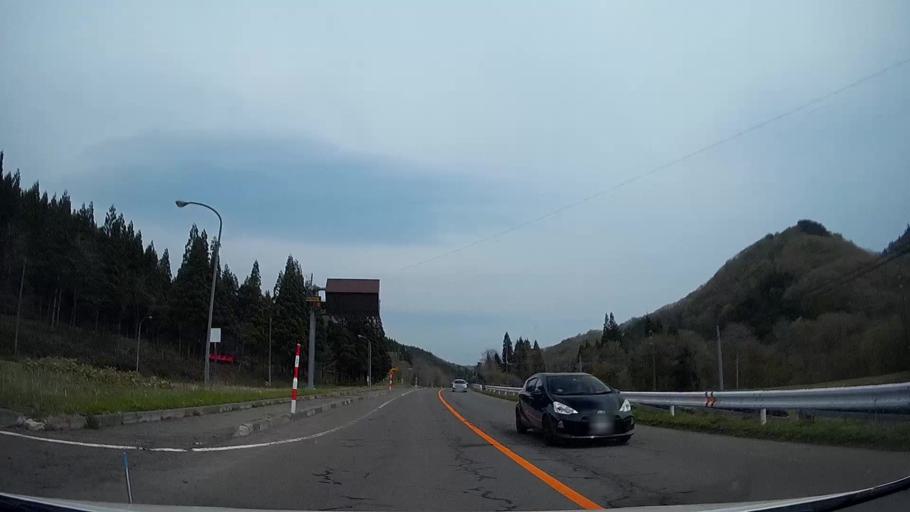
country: JP
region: Akita
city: Hanawa
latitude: 40.3691
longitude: 140.8677
